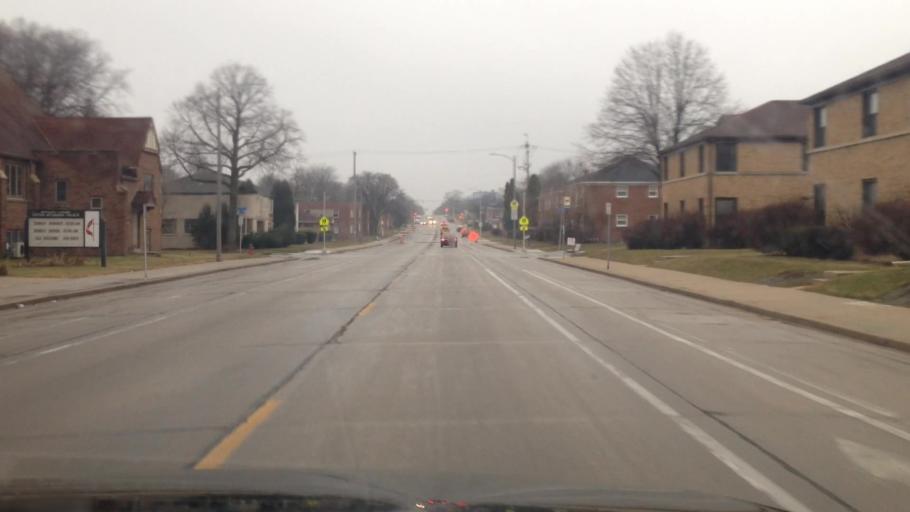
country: US
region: Wisconsin
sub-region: Milwaukee County
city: Wauwatosa
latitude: 43.0681
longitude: -88.0031
